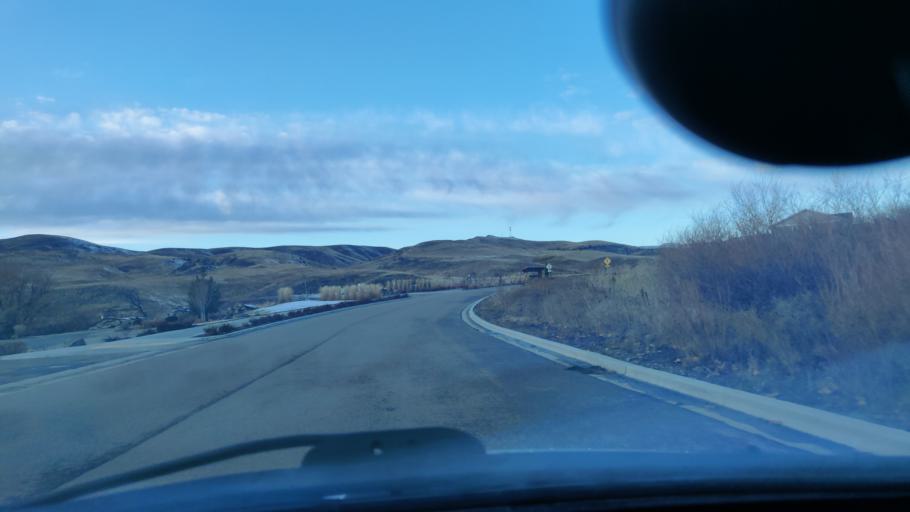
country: US
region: Idaho
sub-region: Ada County
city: Eagle
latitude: 43.7769
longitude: -116.2618
